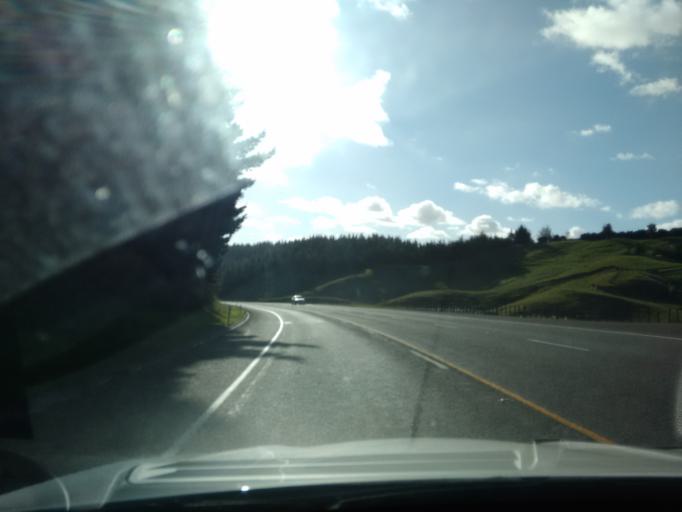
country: NZ
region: Manawatu-Wanganui
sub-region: Wanganui District
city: Wanganui
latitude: -39.8340
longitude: 174.9082
